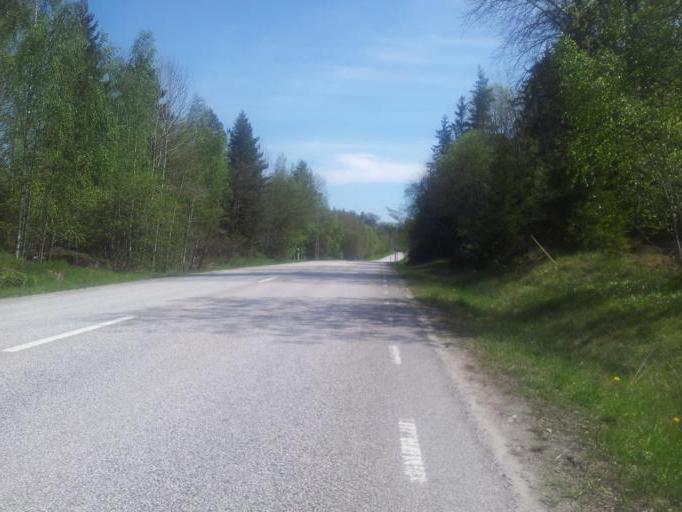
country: SE
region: Uppsala
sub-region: Knivsta Kommun
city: Knivsta
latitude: 59.8544
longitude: 17.8833
